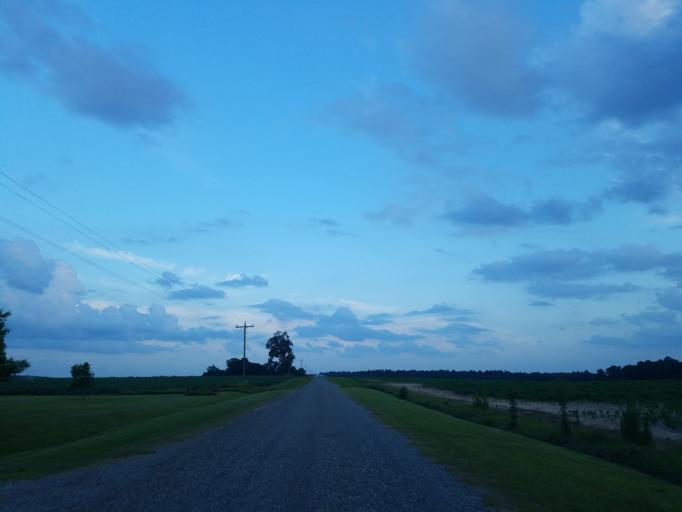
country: US
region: Georgia
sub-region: Dooly County
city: Vienna
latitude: 32.1629
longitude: -83.7317
